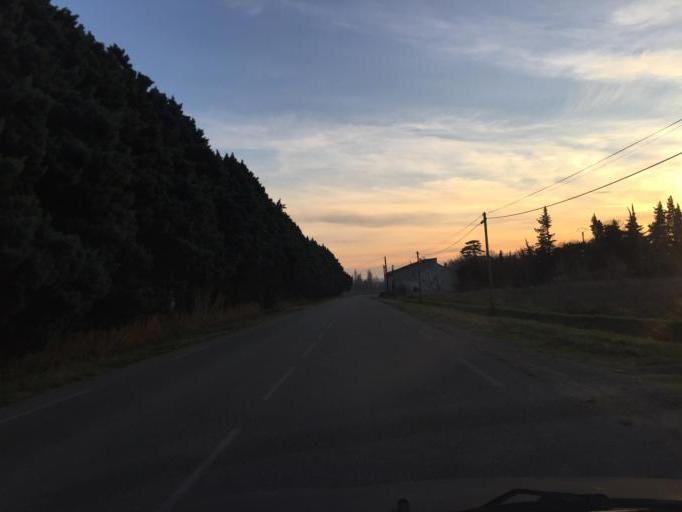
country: FR
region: Provence-Alpes-Cote d'Azur
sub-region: Departement du Vaucluse
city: Jonquieres
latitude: 44.1037
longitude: 4.8922
